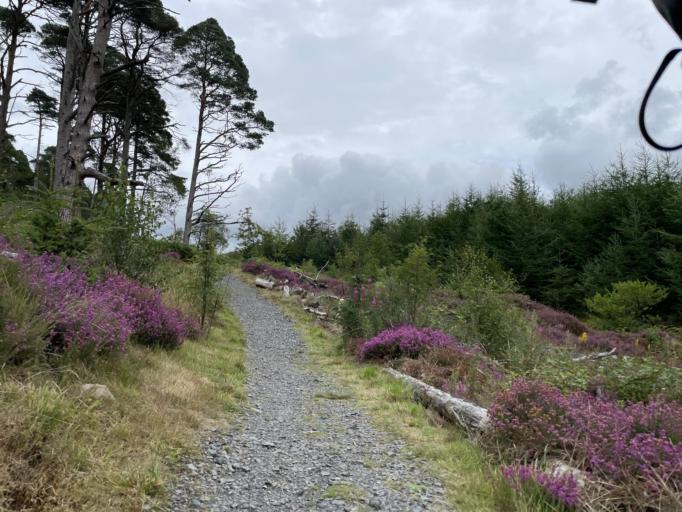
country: GB
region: Scotland
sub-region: Dumfries and Galloway
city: Newton Stewart
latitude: 55.0826
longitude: -4.4985
